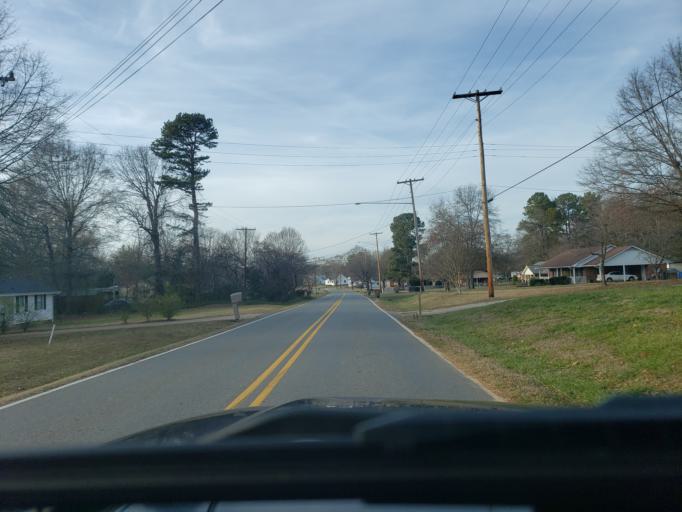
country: US
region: North Carolina
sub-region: Cleveland County
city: Shelby
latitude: 35.2770
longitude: -81.5069
